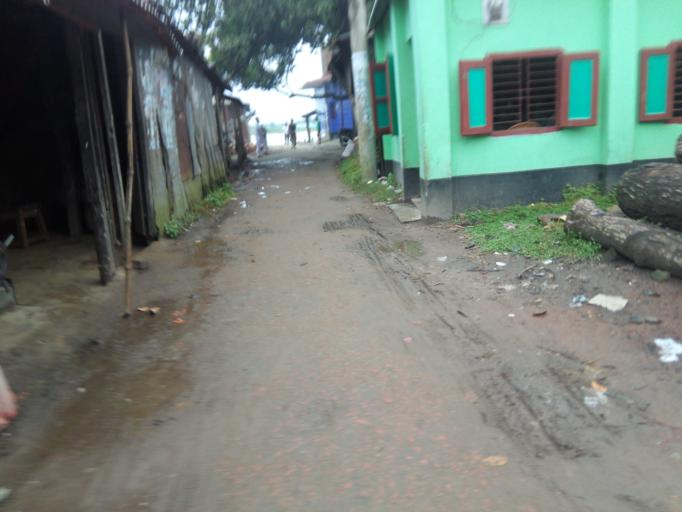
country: BD
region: Khulna
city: Kalia
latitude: 23.2145
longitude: 89.6965
